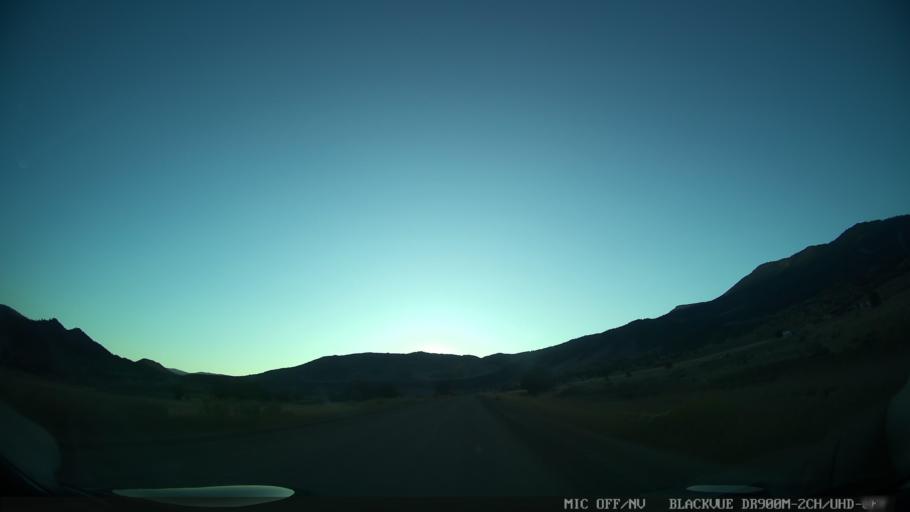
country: US
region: Colorado
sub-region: Eagle County
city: Edwards
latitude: 39.9000
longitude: -106.6019
